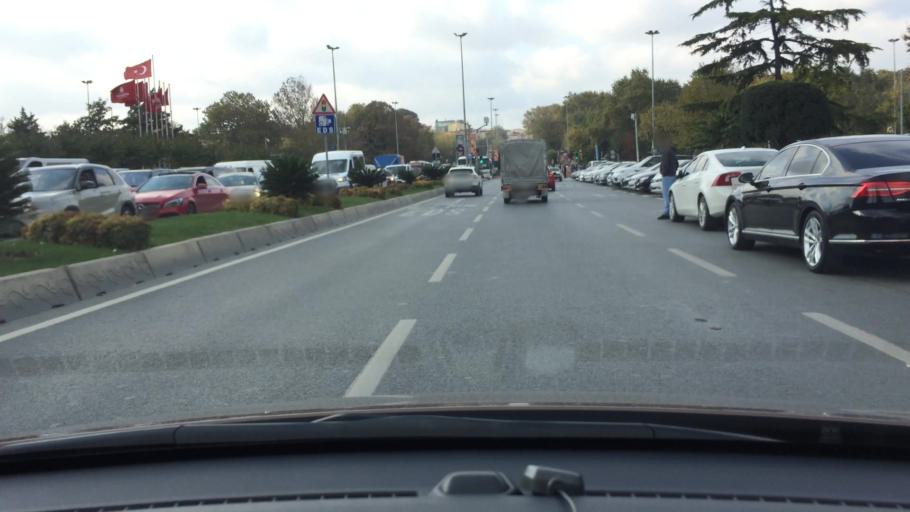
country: TR
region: Istanbul
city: Istanbul
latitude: 41.0139
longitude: 28.9557
